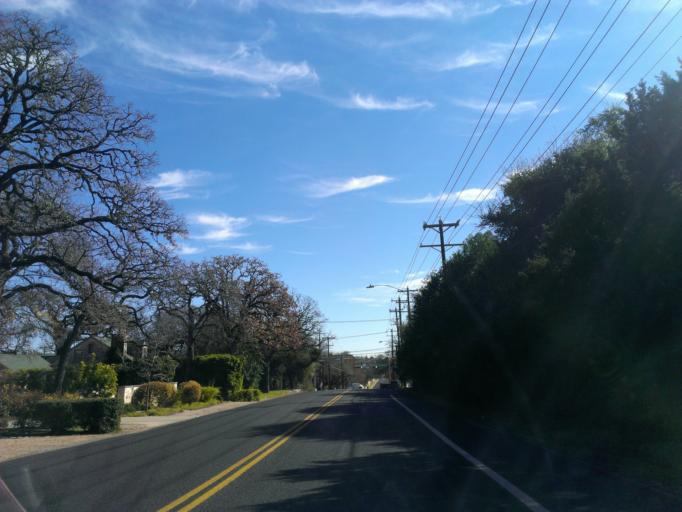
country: US
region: Texas
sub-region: Travis County
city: Rollingwood
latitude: 30.2911
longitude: -97.7732
